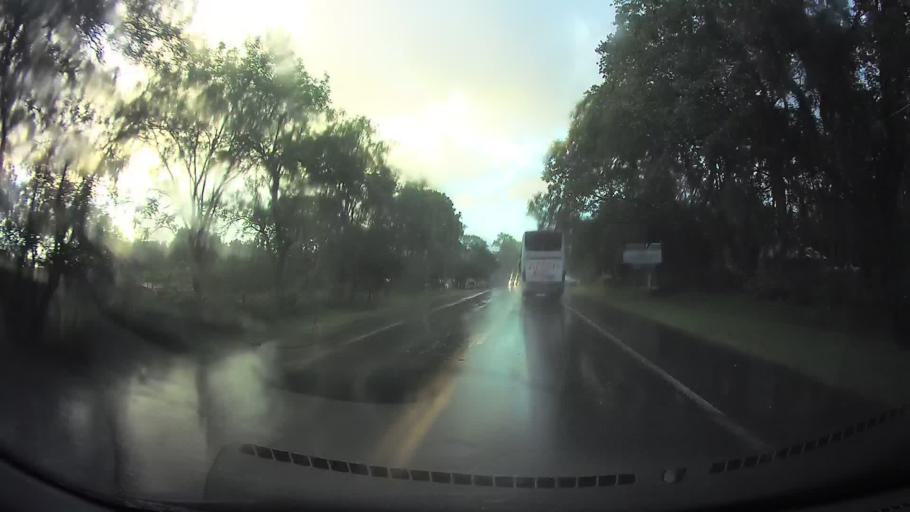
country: PY
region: Paraguari
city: Yaguaron
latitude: -25.5892
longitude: -57.2303
